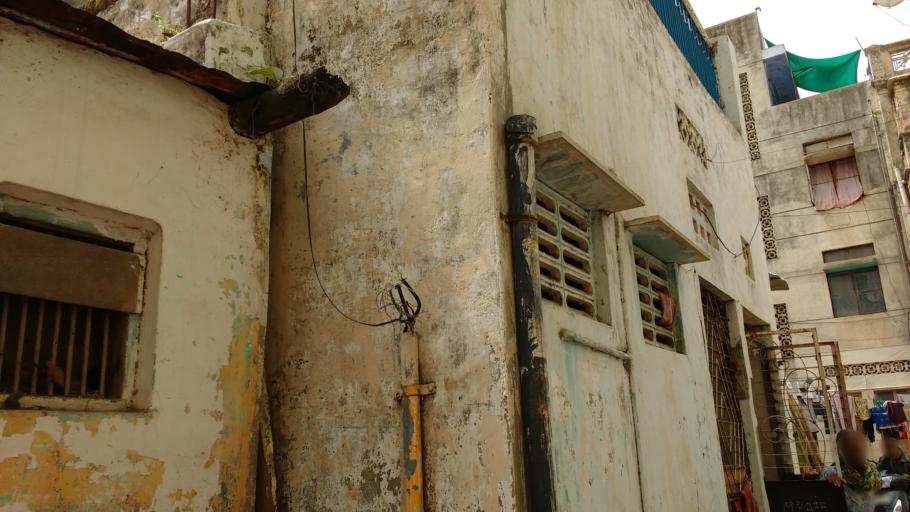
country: IN
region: Gujarat
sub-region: Ahmadabad
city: Ahmedabad
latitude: 23.0232
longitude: 72.5836
